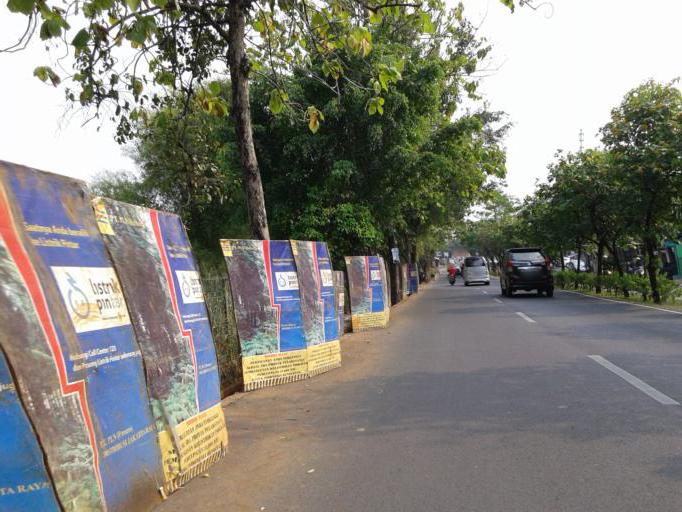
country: ID
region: West Java
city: Pamulang
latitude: -6.3079
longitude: 106.7814
